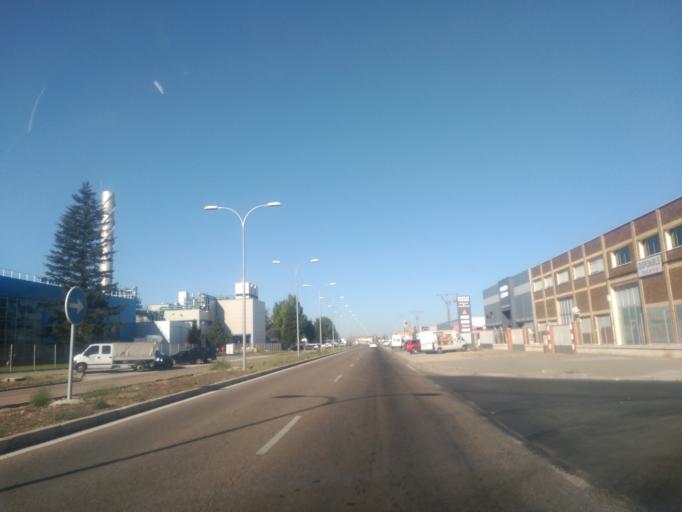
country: ES
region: Castille and Leon
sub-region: Provincia de Burgos
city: Aranda de Duero
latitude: 41.6651
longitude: -3.7084
